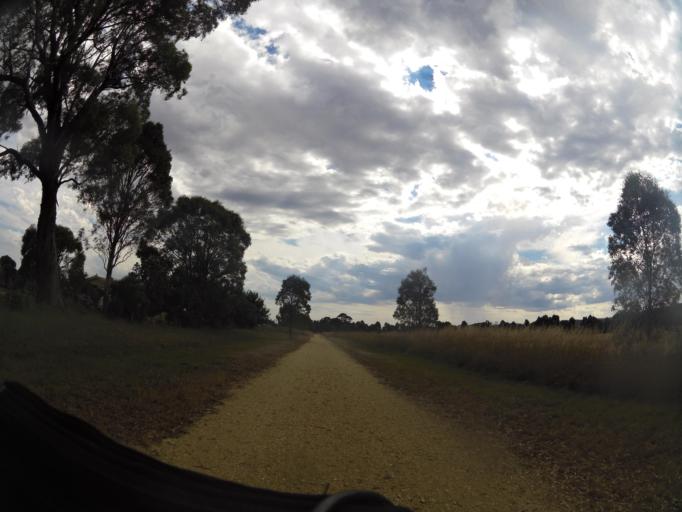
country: AU
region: Victoria
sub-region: Wellington
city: Heyfield
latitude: -38.0477
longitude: 146.6351
